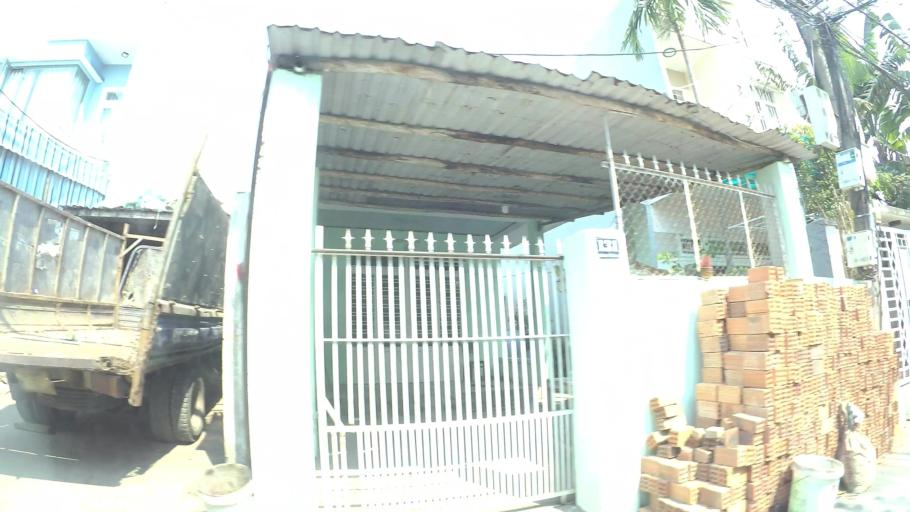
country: VN
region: Da Nang
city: Cam Le
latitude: 16.0123
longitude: 108.1998
